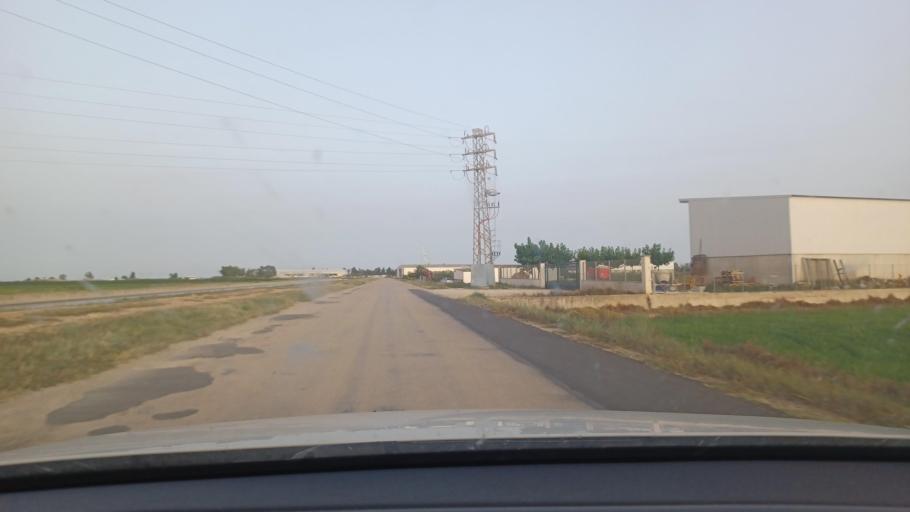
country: ES
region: Catalonia
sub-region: Provincia de Tarragona
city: Amposta
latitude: 40.7038
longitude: 0.5952
